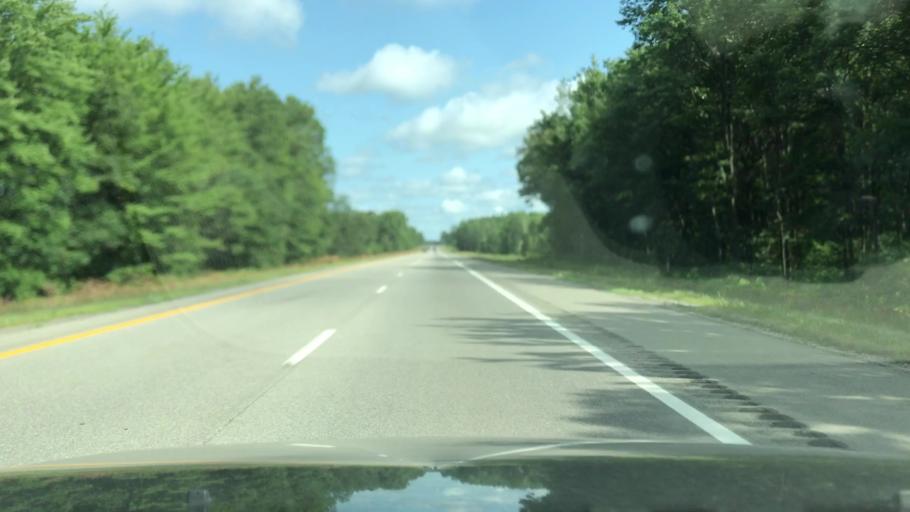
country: US
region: Michigan
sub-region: Montcalm County
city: Howard City
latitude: 43.5140
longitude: -85.4860
